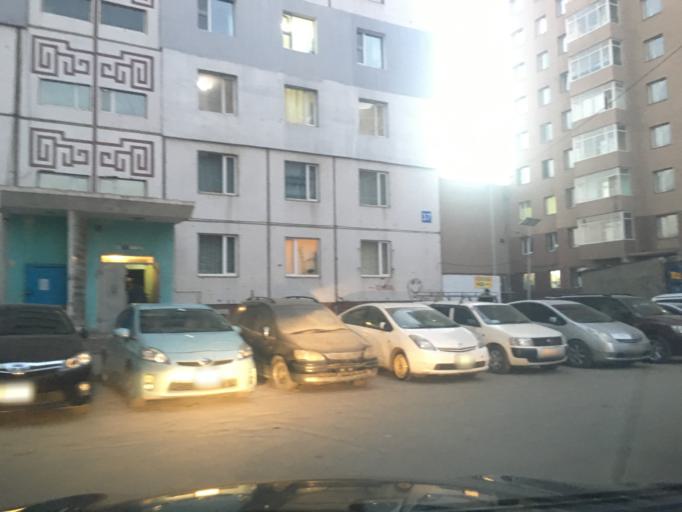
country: MN
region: Ulaanbaatar
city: Ulaanbaatar
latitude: 47.9191
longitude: 106.8901
